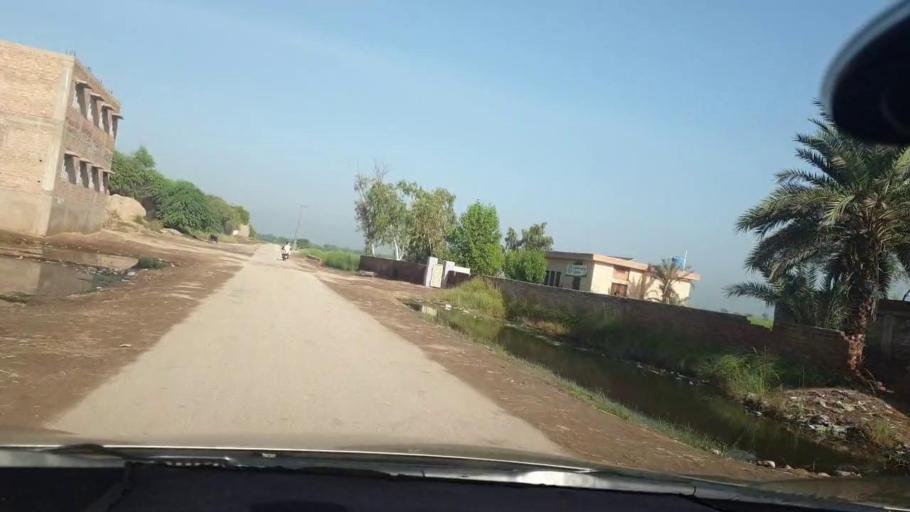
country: PK
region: Sindh
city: Kambar
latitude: 27.6553
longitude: 68.0307
